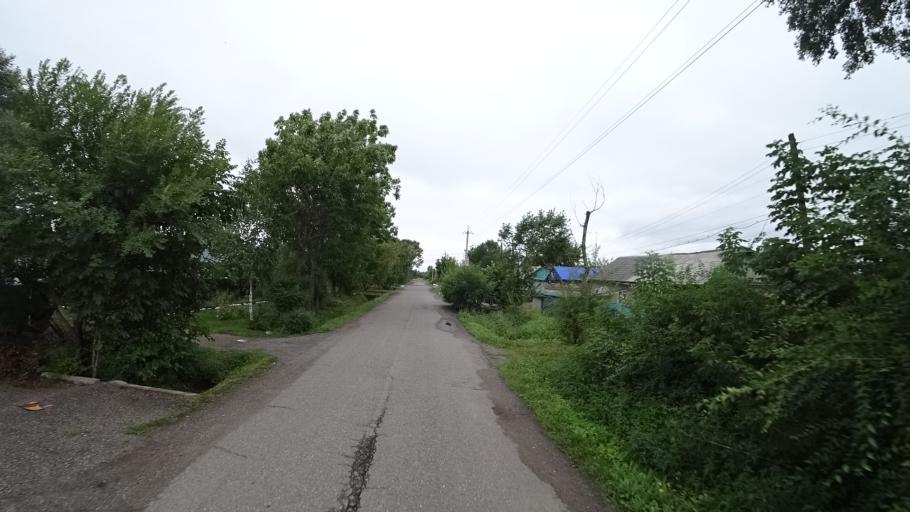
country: RU
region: Primorskiy
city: Chernigovka
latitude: 44.3434
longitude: 132.5843
